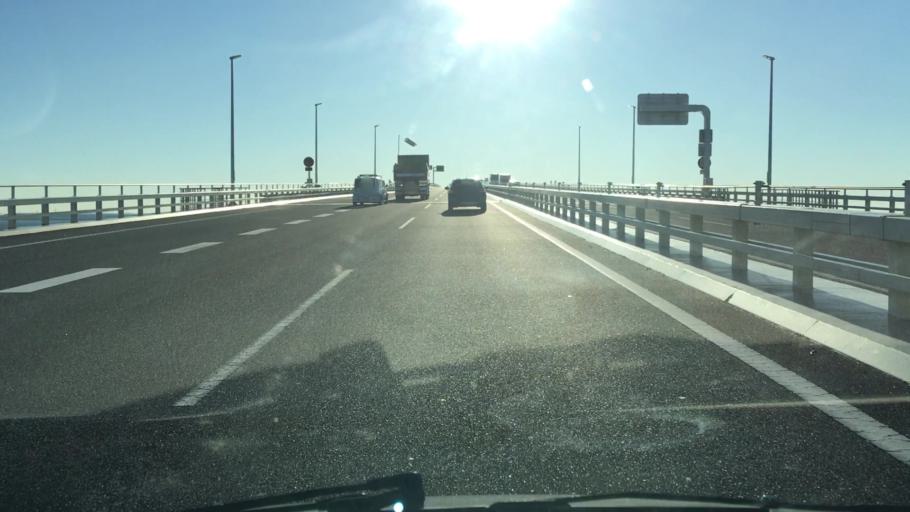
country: JP
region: Chiba
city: Kisarazu
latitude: 35.4598
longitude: 139.8811
